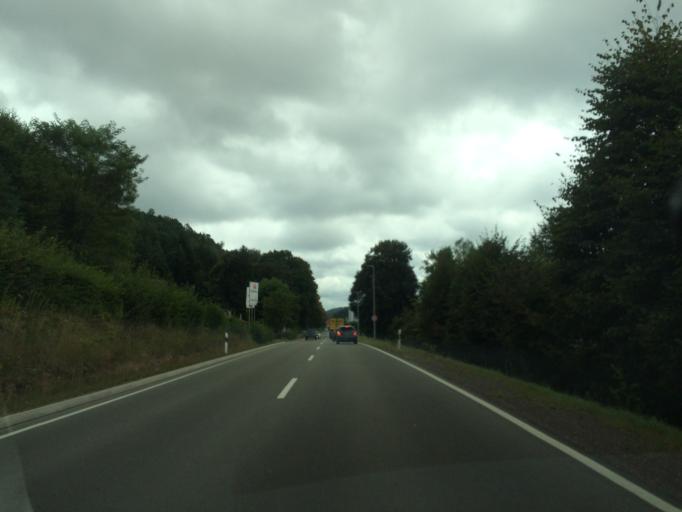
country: DE
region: Rheinland-Pfalz
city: Dahn
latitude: 49.1598
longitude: 7.7682
